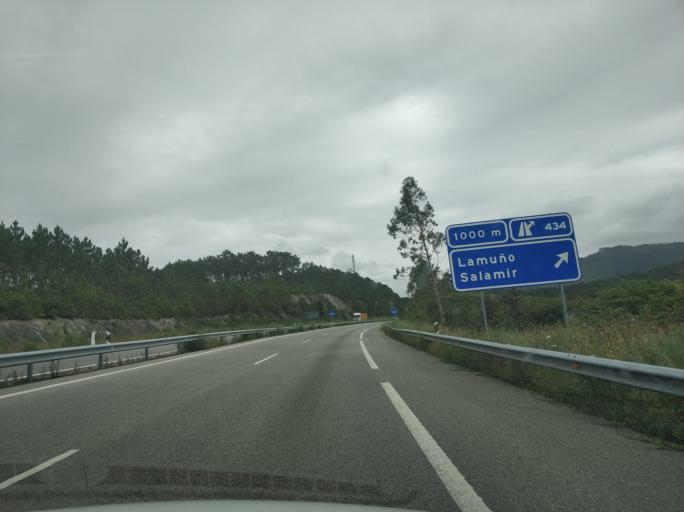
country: ES
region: Asturias
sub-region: Province of Asturias
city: Cudillero
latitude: 43.5671
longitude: -6.2178
